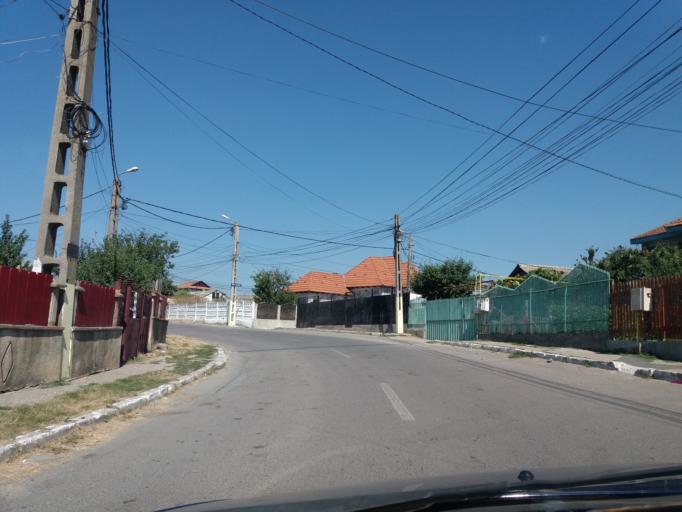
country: RO
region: Constanta
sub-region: Comuna Navodari
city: Navodari
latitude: 44.3303
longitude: 28.6107
